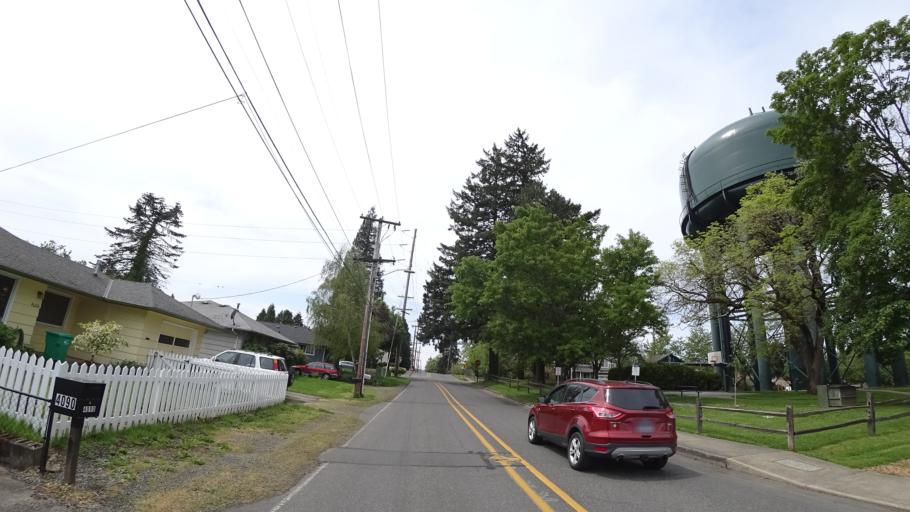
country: US
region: Oregon
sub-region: Clackamas County
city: Milwaukie
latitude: 45.4514
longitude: -122.6215
